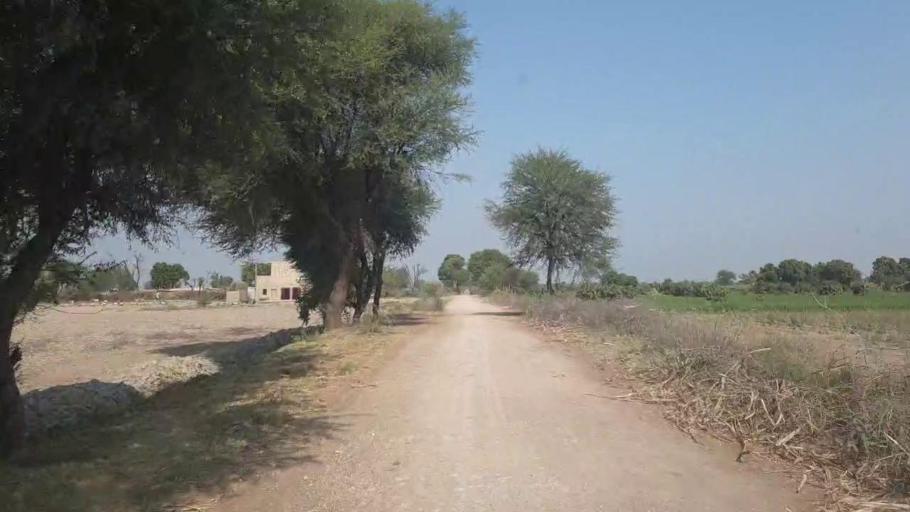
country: PK
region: Sindh
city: Tando Allahyar
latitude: 25.4497
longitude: 68.8499
